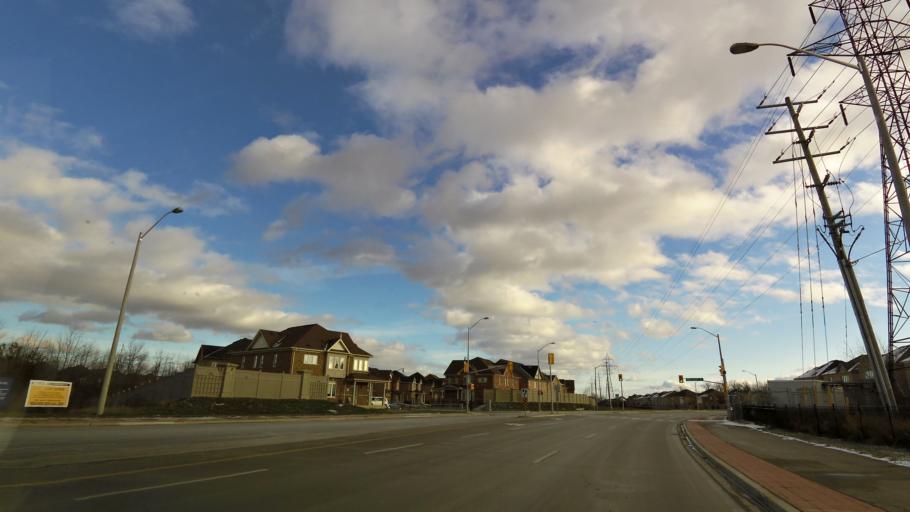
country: CA
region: Ontario
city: Brampton
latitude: 43.6622
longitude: -79.7839
